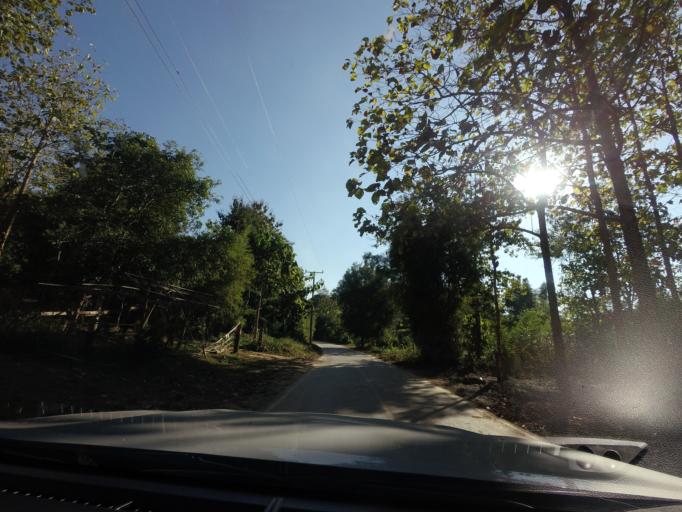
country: TH
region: Lampang
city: Chae Hom
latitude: 18.5980
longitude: 99.6269
